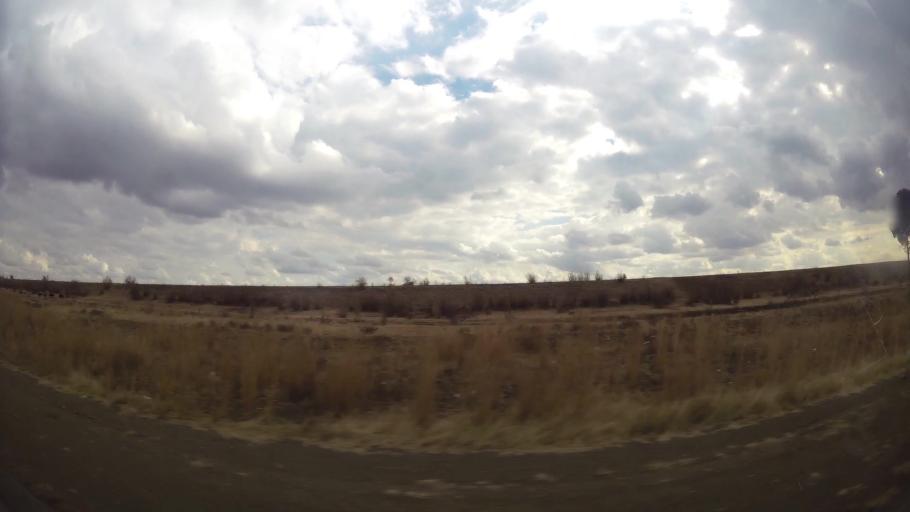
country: ZA
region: Orange Free State
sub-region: Fezile Dabi District Municipality
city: Sasolburg
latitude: -26.8728
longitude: 27.8872
